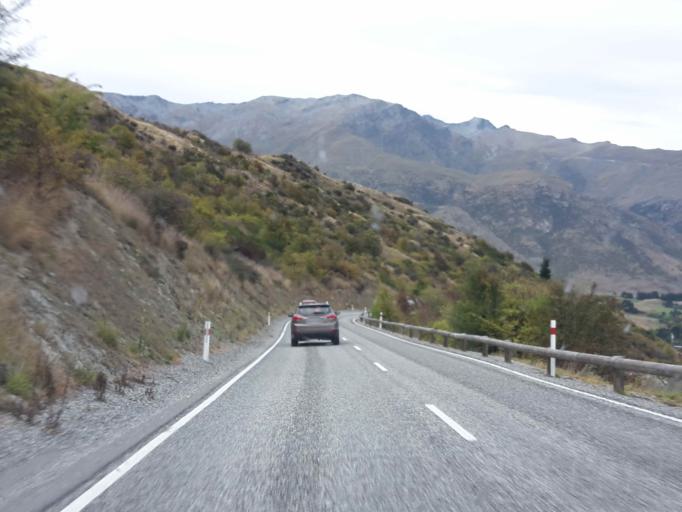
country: NZ
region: Otago
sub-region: Queenstown-Lakes District
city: Arrowtown
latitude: -44.9756
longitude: 168.8643
